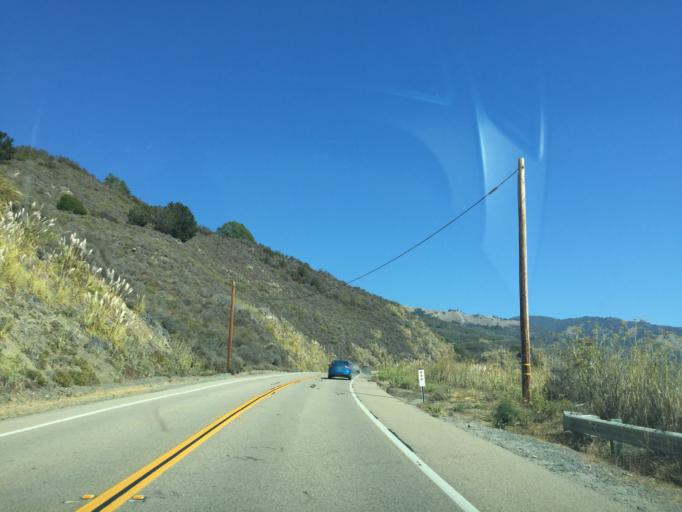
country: US
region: California
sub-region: Monterey County
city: Greenfield
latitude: 36.0214
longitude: -121.5633
